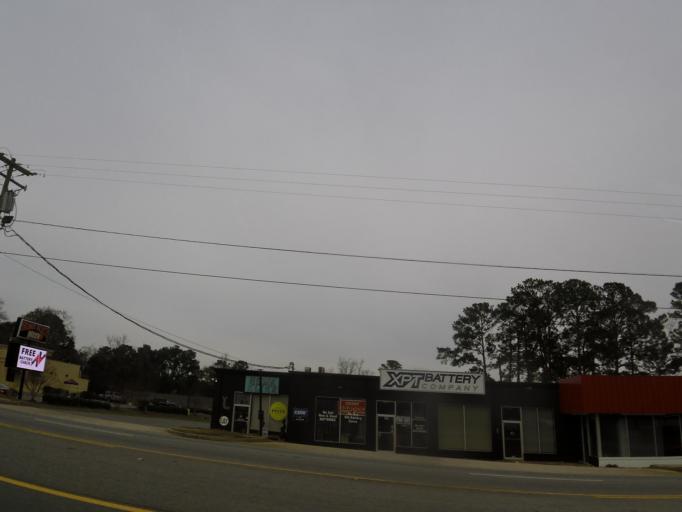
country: US
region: Georgia
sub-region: Grady County
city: Cairo
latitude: 30.8803
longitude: -84.1975
